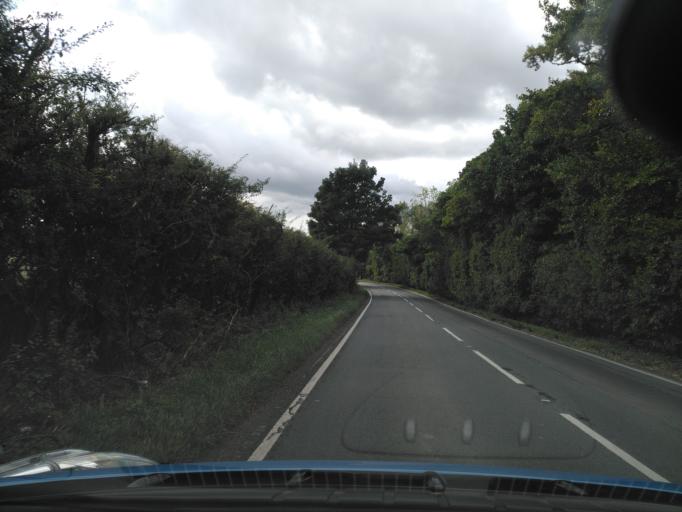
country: GB
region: England
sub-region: Oxfordshire
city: Harwell
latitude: 51.6000
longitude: -1.3213
